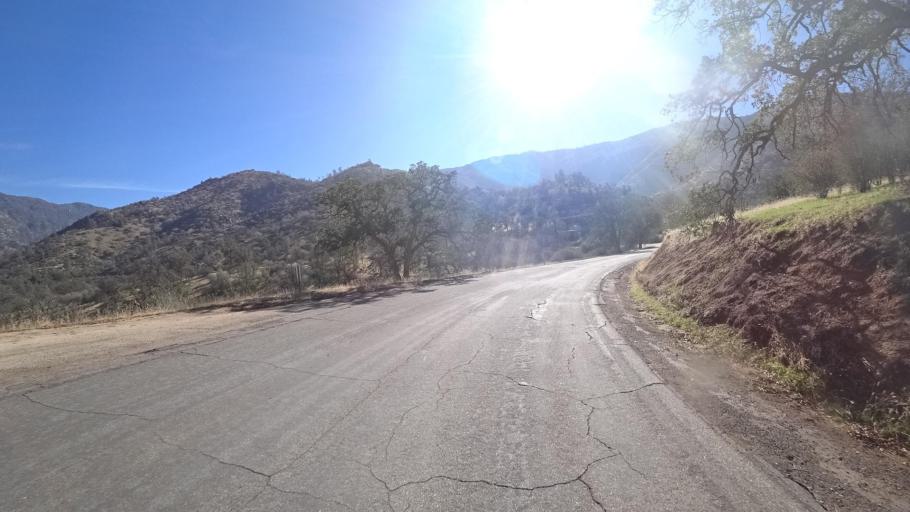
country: US
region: California
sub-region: Kern County
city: Bodfish
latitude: 35.5328
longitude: -118.6284
